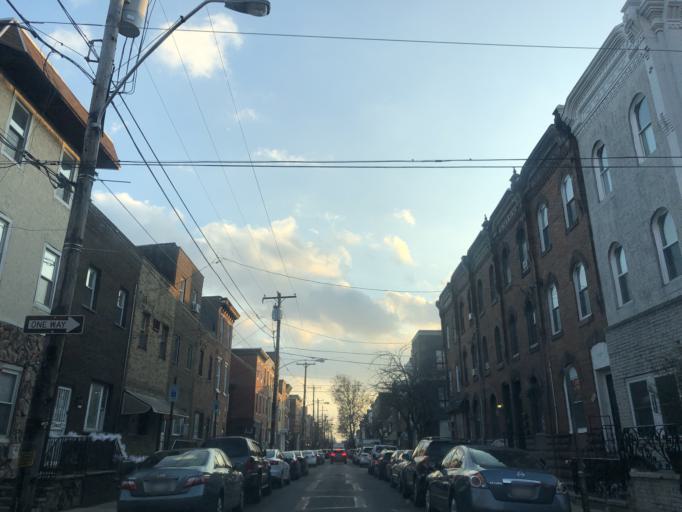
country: US
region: Pennsylvania
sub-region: Philadelphia County
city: Philadelphia
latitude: 39.9305
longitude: -75.1614
